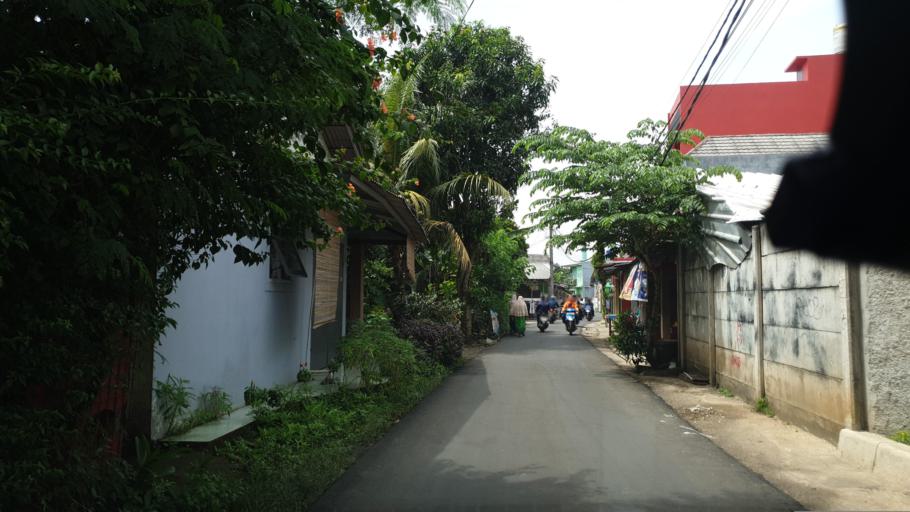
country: ID
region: West Java
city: Sawangan
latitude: -6.3719
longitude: 106.7618
